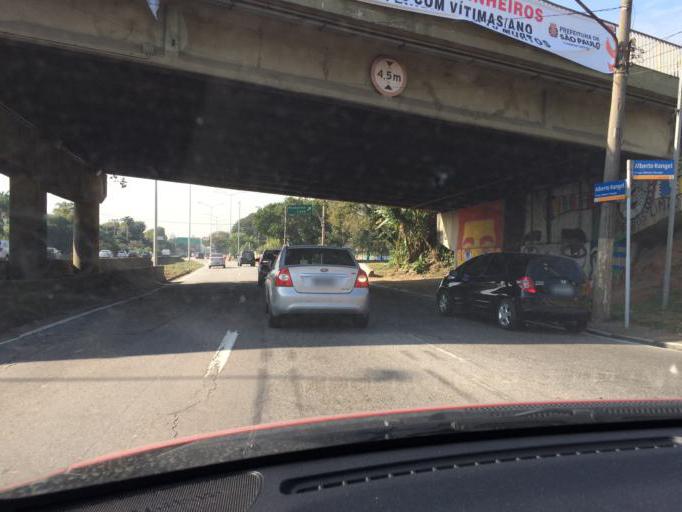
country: BR
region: Sao Paulo
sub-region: Sao Paulo
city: Sao Paulo
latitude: -23.5591
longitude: -46.7122
